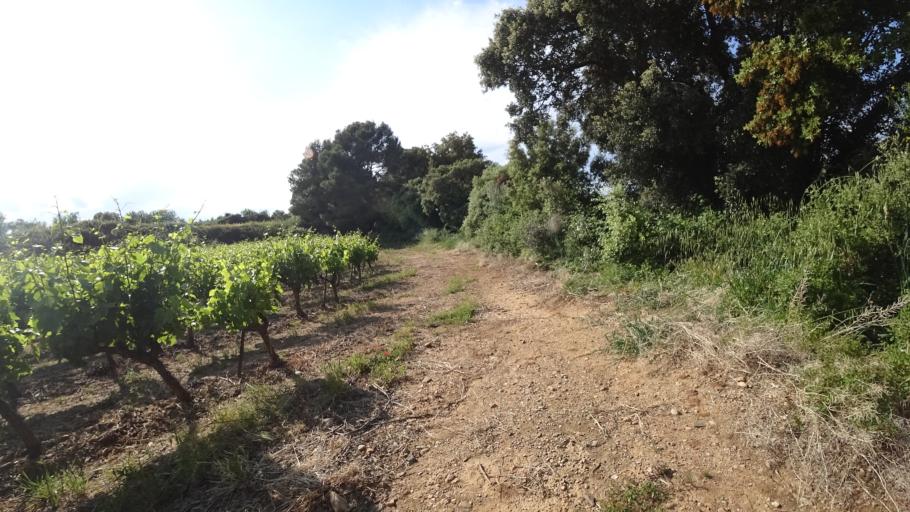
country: FR
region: Languedoc-Roussillon
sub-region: Departement de l'Aude
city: Canet
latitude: 43.2586
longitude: 2.8331
